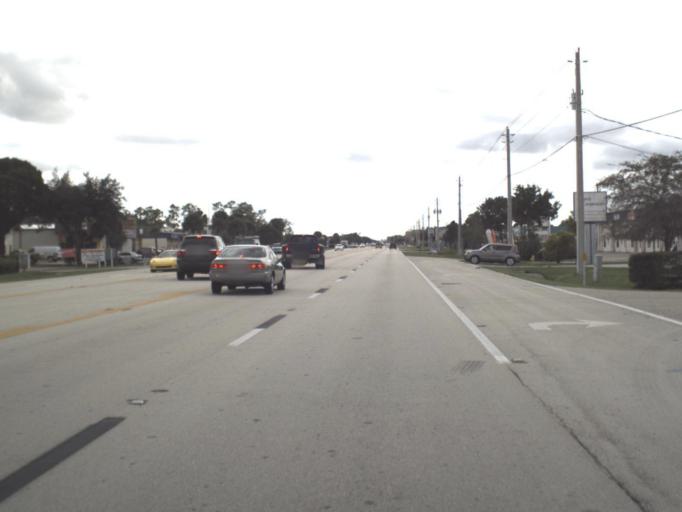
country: US
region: Florida
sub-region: Lee County
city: Villas
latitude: 26.5595
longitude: -81.8530
